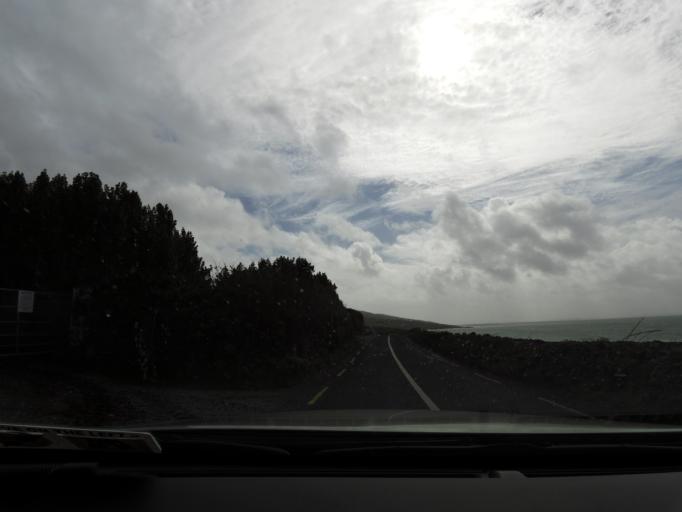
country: IE
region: Connaught
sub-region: County Galway
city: Bearna
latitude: 53.0938
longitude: -9.3062
